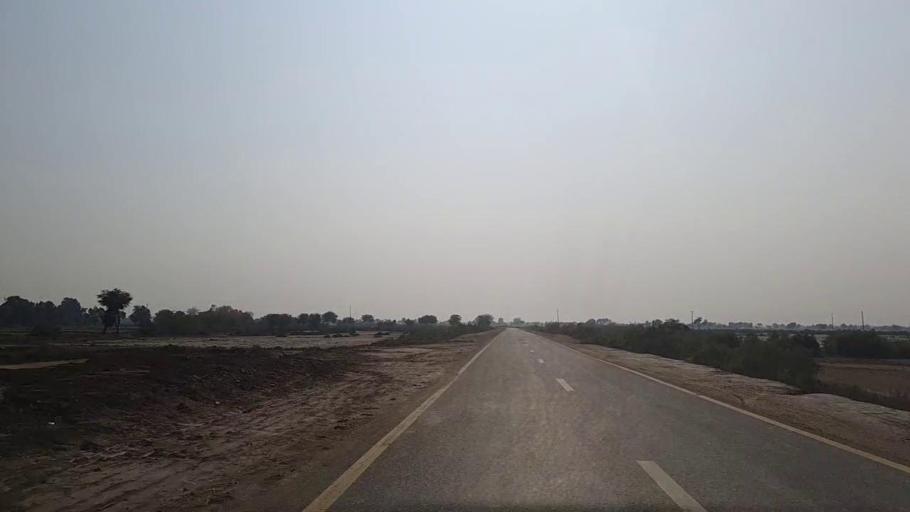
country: PK
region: Sindh
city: Jam Sahib
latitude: 26.3681
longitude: 68.5359
